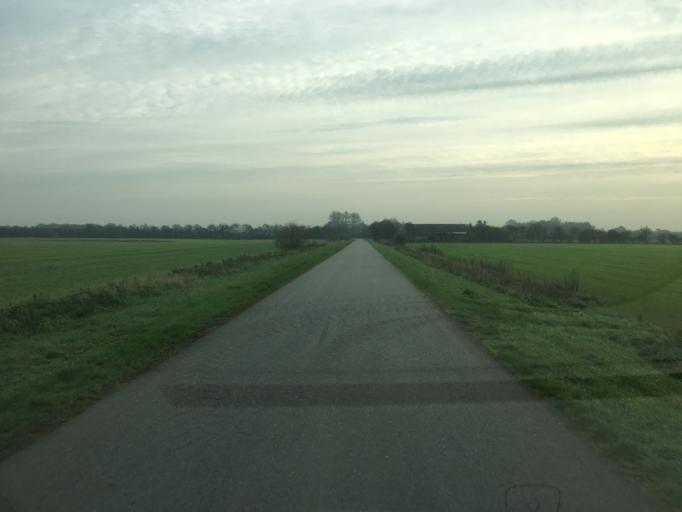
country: DK
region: South Denmark
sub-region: Tonder Kommune
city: Logumkloster
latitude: 55.1018
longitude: 9.0367
